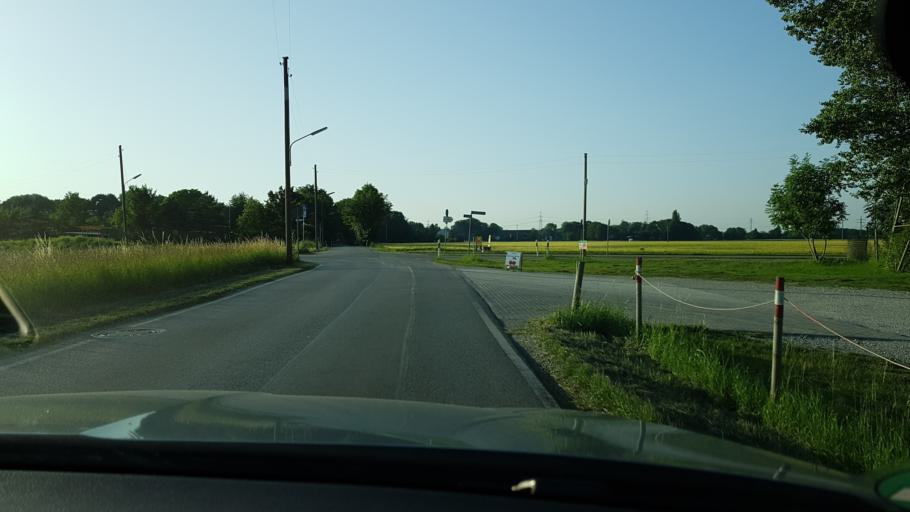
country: DE
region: Bavaria
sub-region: Upper Bavaria
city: Unterfoehring
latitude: 48.1613
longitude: 11.6506
